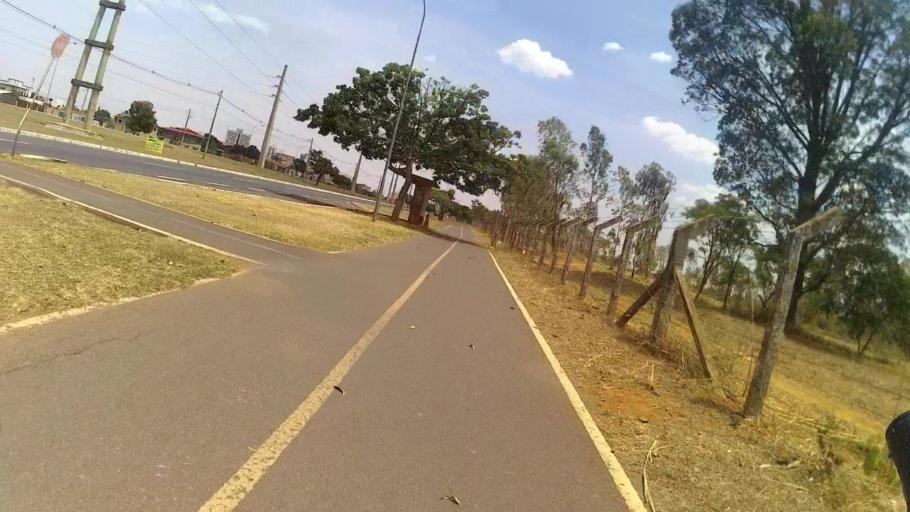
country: BR
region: Federal District
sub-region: Brasilia
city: Brasilia
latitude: -15.8732
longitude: -48.0546
